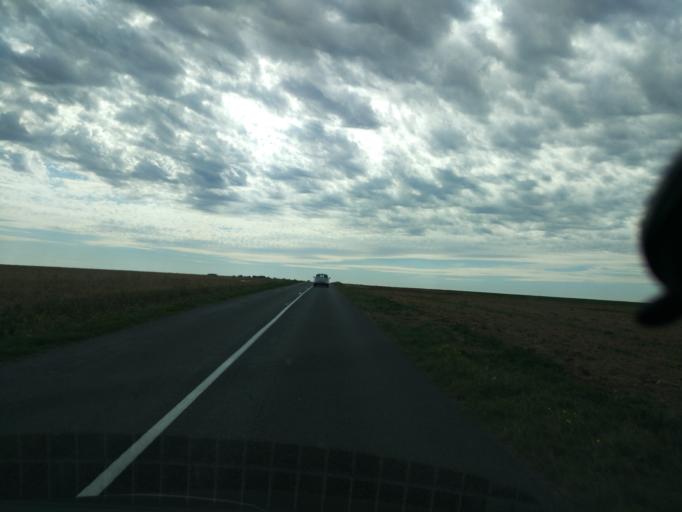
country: FR
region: Ile-de-France
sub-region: Departement de l'Essonne
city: Gometz-la-Ville
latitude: 48.6615
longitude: 2.1260
